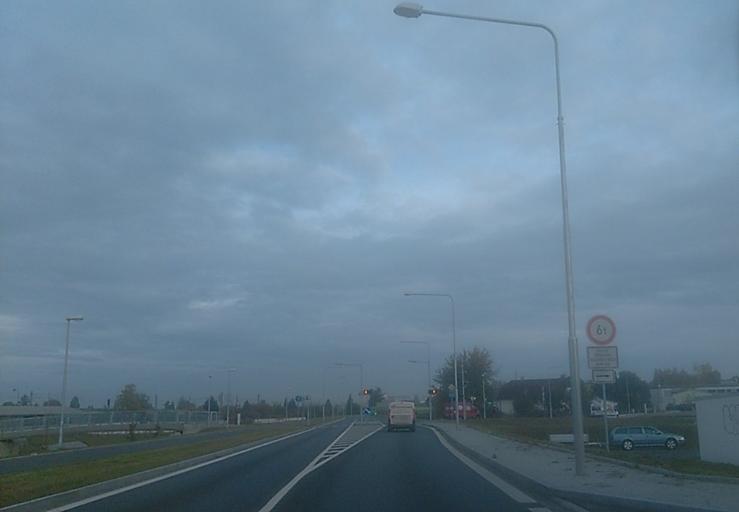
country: CZ
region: Jihocesky
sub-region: Okres Ceske Budejovice
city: Ceske Budejovice
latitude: 48.9832
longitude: 14.4869
